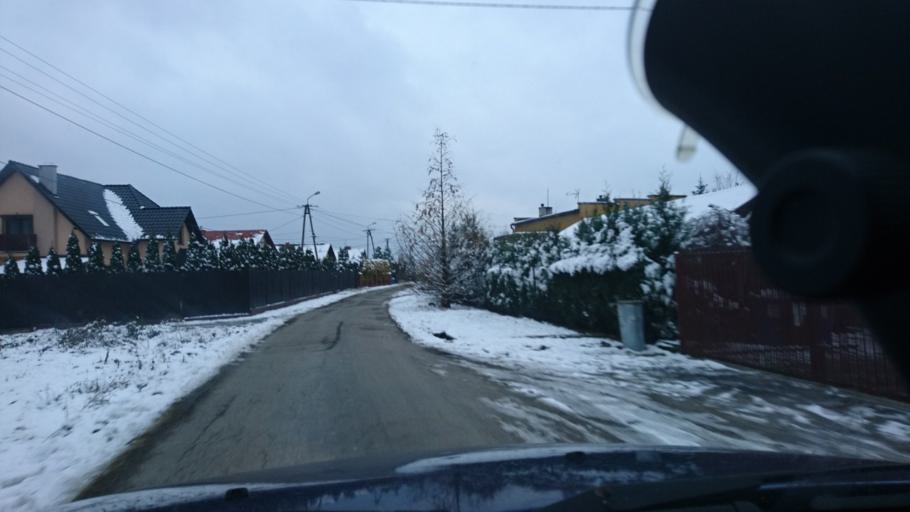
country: PL
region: Silesian Voivodeship
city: Janowice
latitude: 49.8660
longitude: 19.1109
